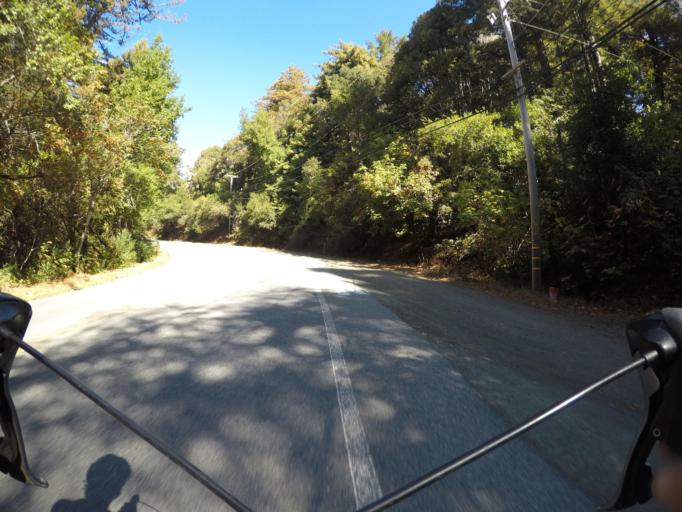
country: US
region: California
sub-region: San Mateo County
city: Portola Valley
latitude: 37.3375
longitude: -122.2692
